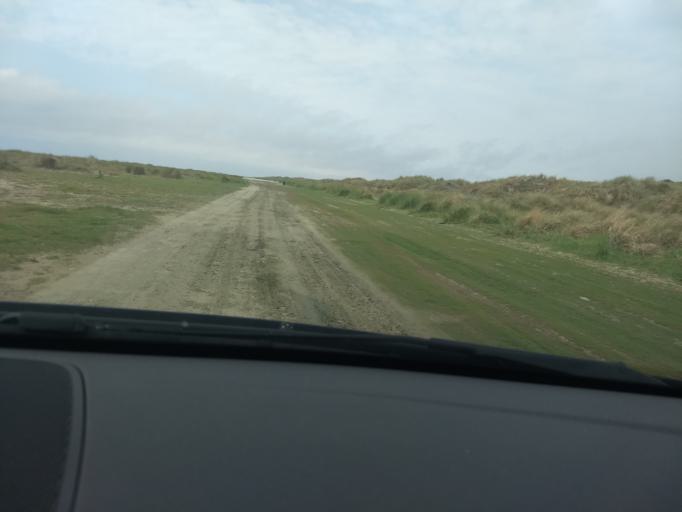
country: DK
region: South Denmark
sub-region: Fano Kommune
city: Nordby
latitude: 55.4083
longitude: 8.3865
